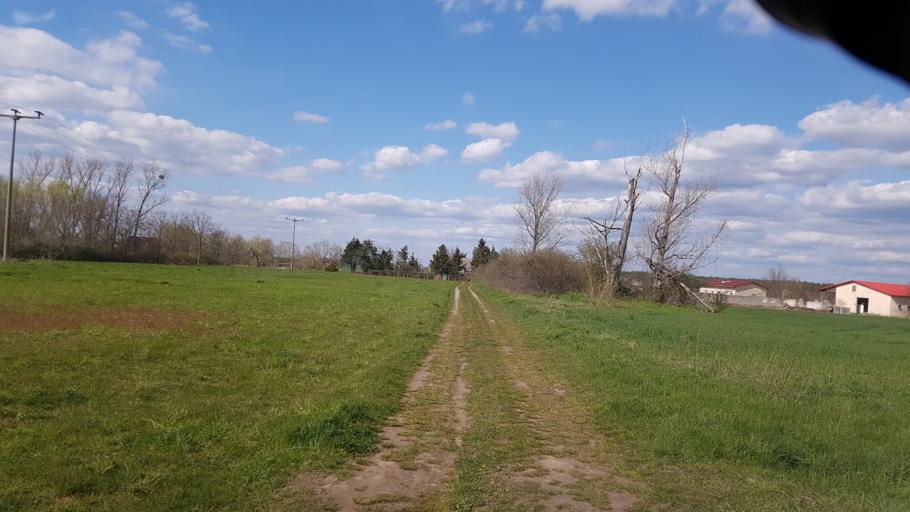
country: DE
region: Brandenburg
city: Muhlberg
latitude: 51.4747
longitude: 13.2713
